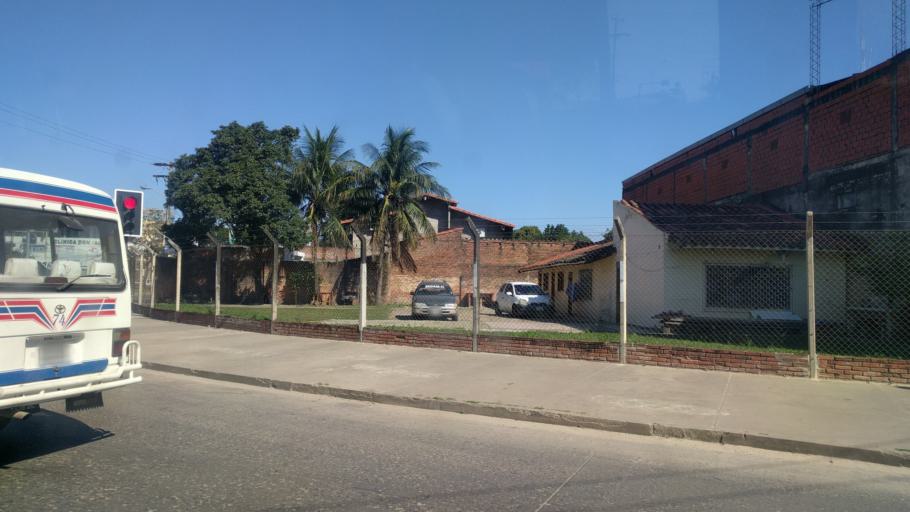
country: BO
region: Santa Cruz
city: Santa Cruz de la Sierra
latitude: -17.7509
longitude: -63.1873
